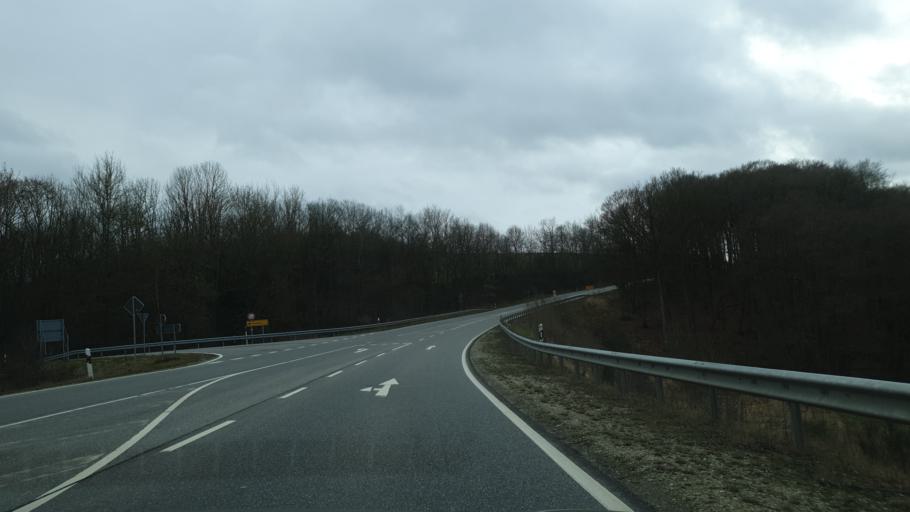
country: DE
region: Rheinland-Pfalz
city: Kratzenburg
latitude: 50.1831
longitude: 7.5712
